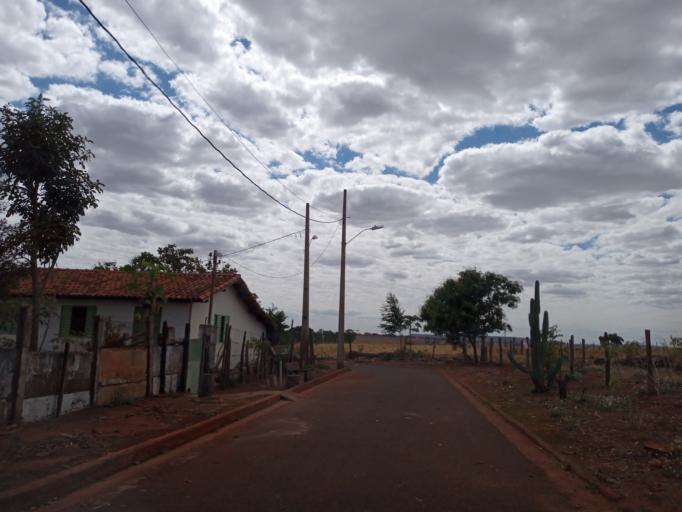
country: BR
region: Minas Gerais
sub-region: Ituiutaba
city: Ituiutaba
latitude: -18.9549
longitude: -49.4496
